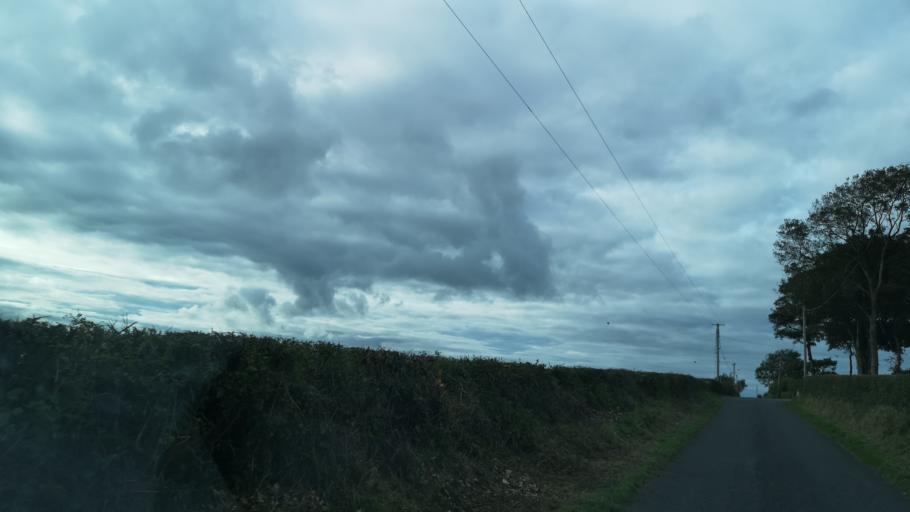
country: IE
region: Connaught
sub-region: County Galway
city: Ballinasloe
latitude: 53.3685
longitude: -8.1620
